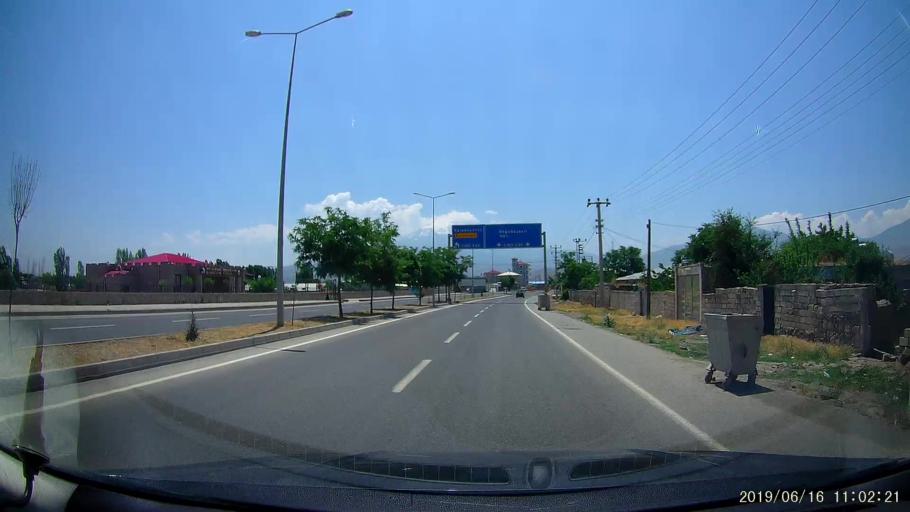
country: TR
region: Igdir
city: Igdir
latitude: 39.9075
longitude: 44.0587
